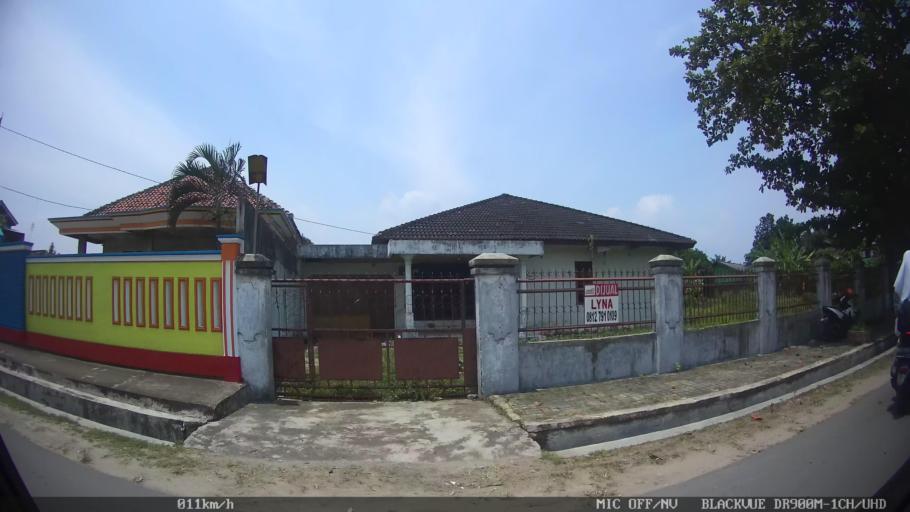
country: ID
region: Lampung
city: Bandarlampung
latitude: -5.4571
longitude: 105.2563
